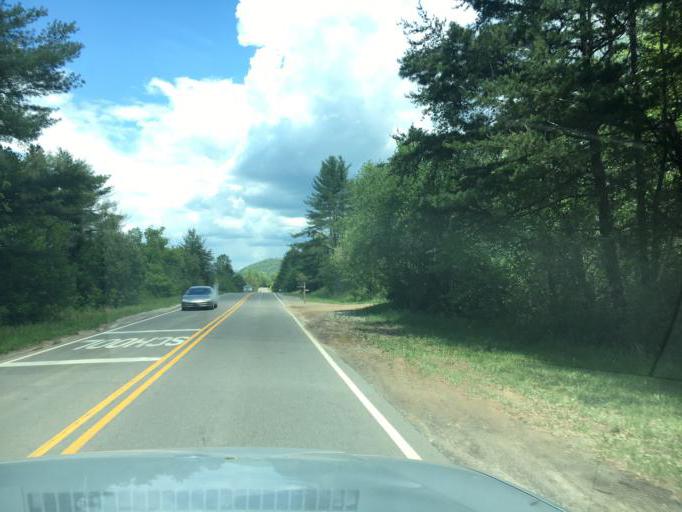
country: US
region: North Carolina
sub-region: Buncombe County
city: Weaverville
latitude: 35.7165
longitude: -82.5596
